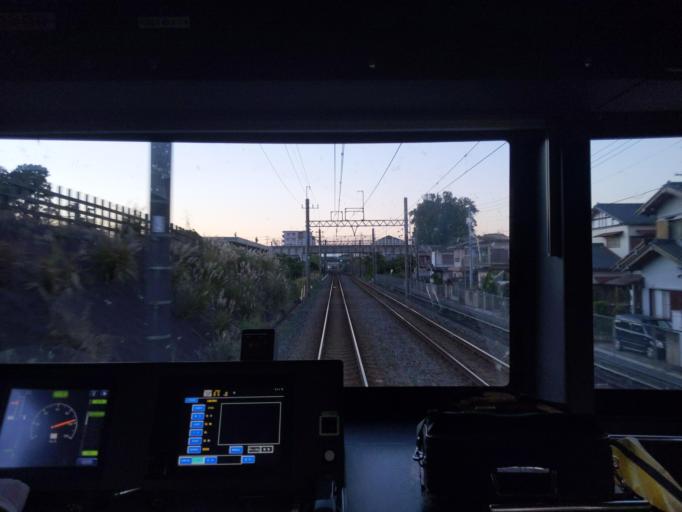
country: JP
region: Chiba
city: Kashiwa
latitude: 35.8262
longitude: 139.9806
